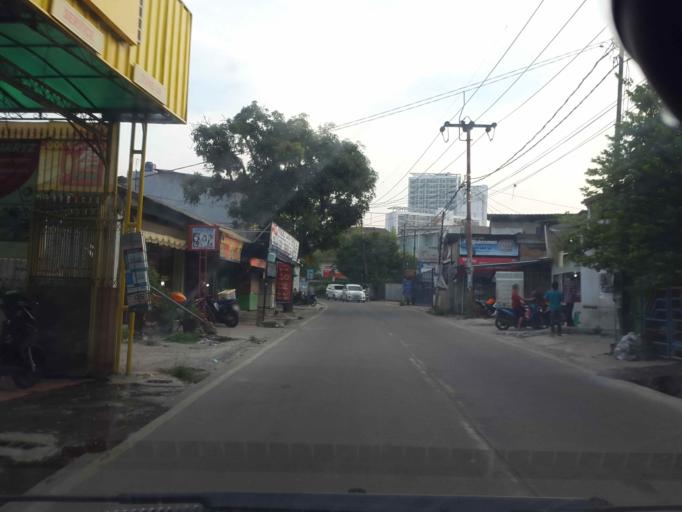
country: ID
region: Banten
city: South Tangerang
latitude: -6.2702
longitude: 106.7426
